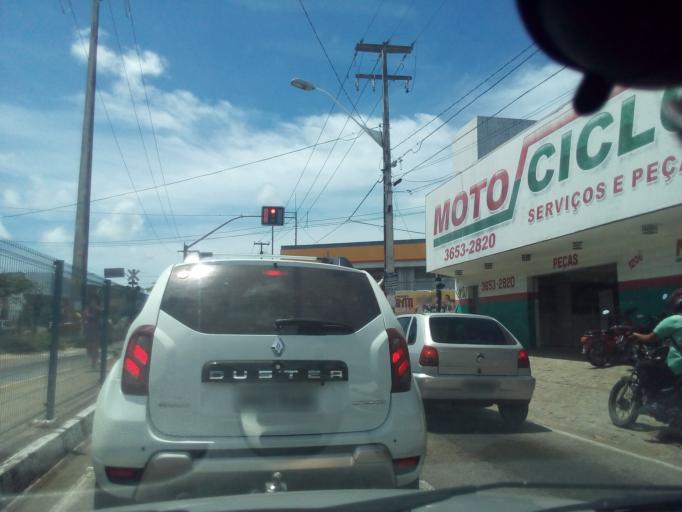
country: BR
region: Rio Grande do Norte
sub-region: Natal
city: Natal
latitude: -5.8043
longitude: -35.2285
